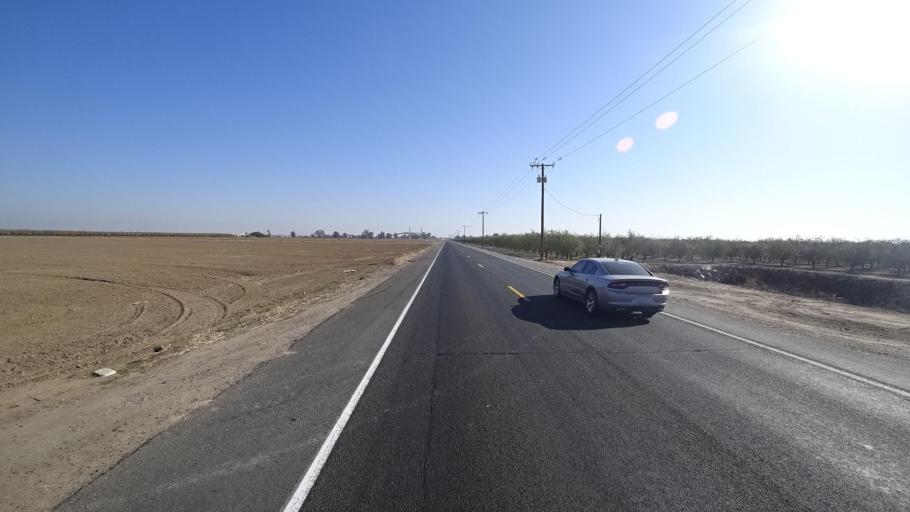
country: US
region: California
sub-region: Kern County
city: McFarland
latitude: 35.7179
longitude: -119.2495
